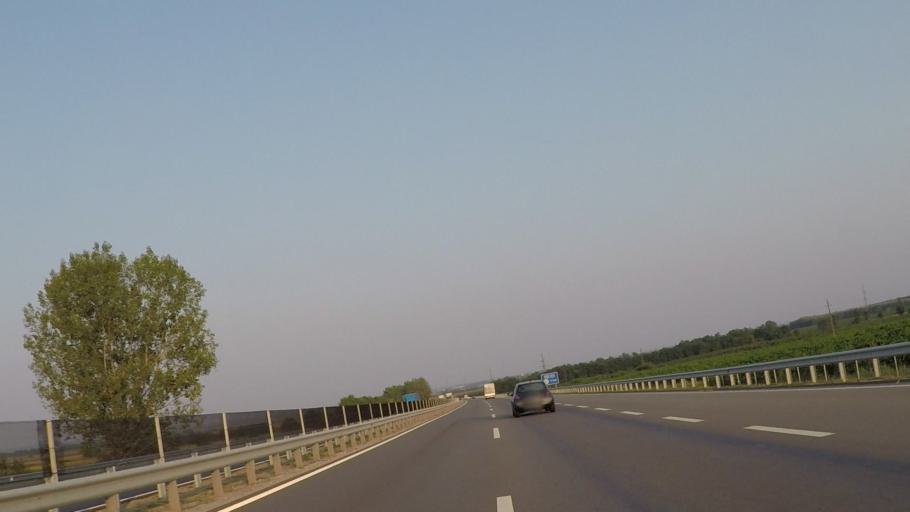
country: HU
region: Pest
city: Cegledbercel
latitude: 47.2213
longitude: 19.6974
